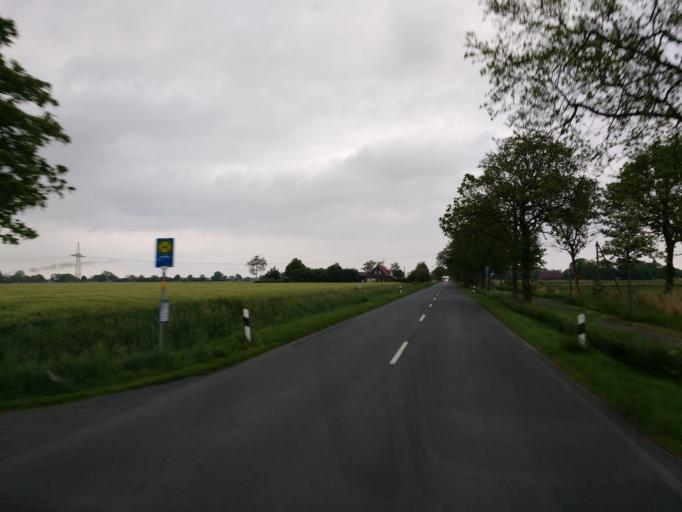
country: DE
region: Lower Saxony
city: Schillig
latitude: 53.6662
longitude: 7.9741
